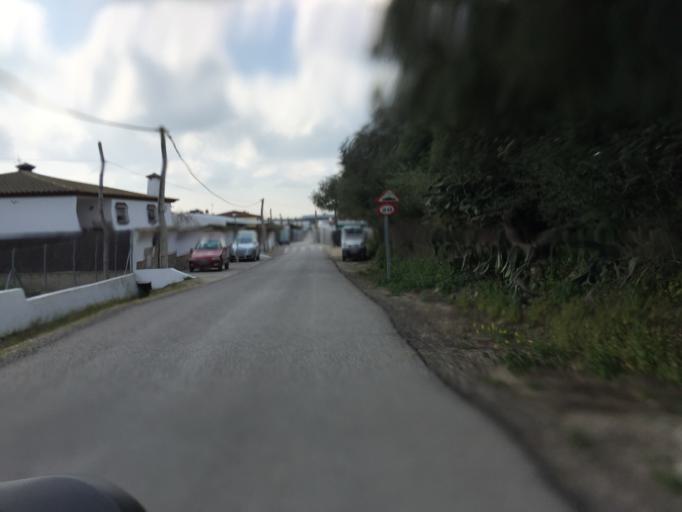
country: ES
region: Andalusia
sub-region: Provincia de Cadiz
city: Benalup-Casas Viejas
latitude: 36.3183
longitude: -5.8844
